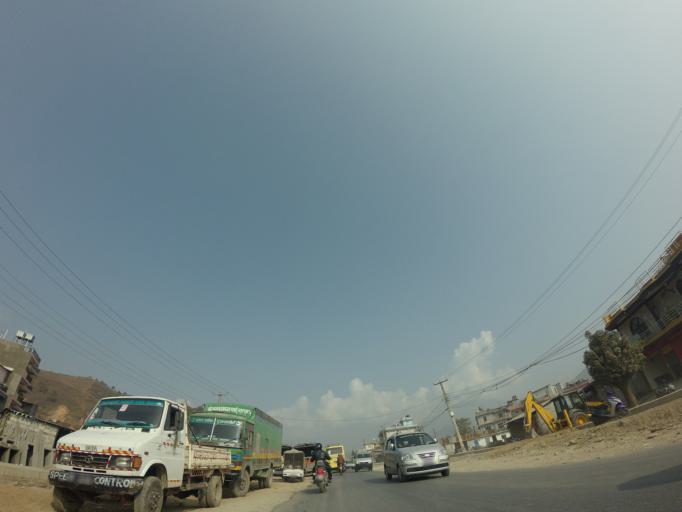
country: NP
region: Western Region
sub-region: Gandaki Zone
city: Pokhara
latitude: 28.2259
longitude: 83.9807
